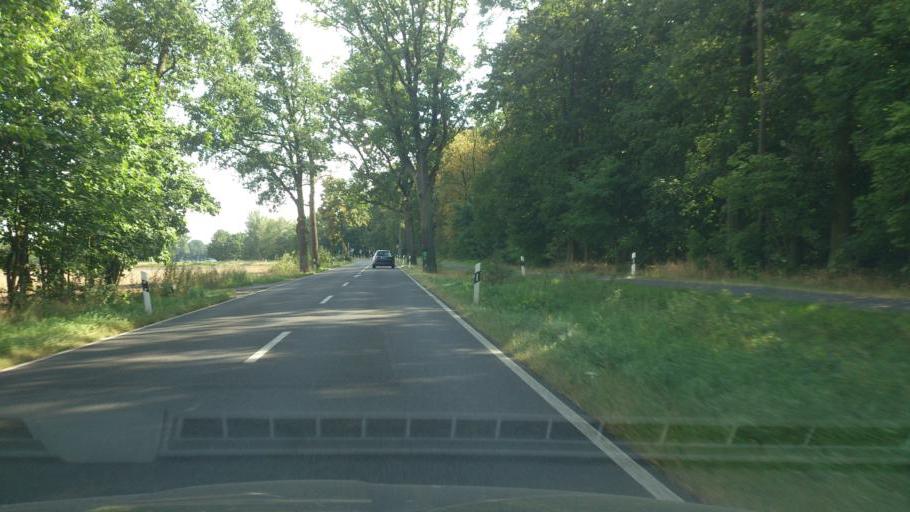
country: DE
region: Brandenburg
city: Stahnsdorf
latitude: 52.3375
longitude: 13.1602
